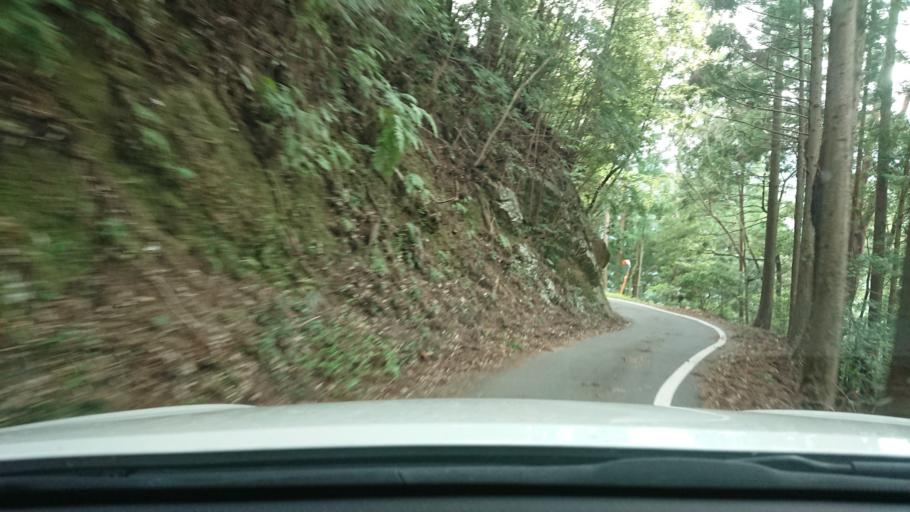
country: JP
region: Tokushima
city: Kamojimacho-jogejima
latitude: 33.8848
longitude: 134.3804
